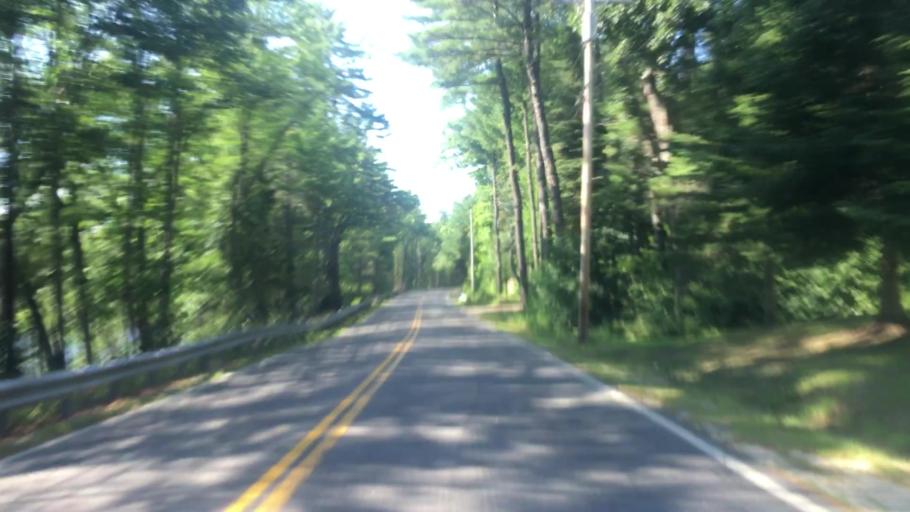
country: US
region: Maine
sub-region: York County
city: Hollis Center
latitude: 43.6578
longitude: -70.5966
